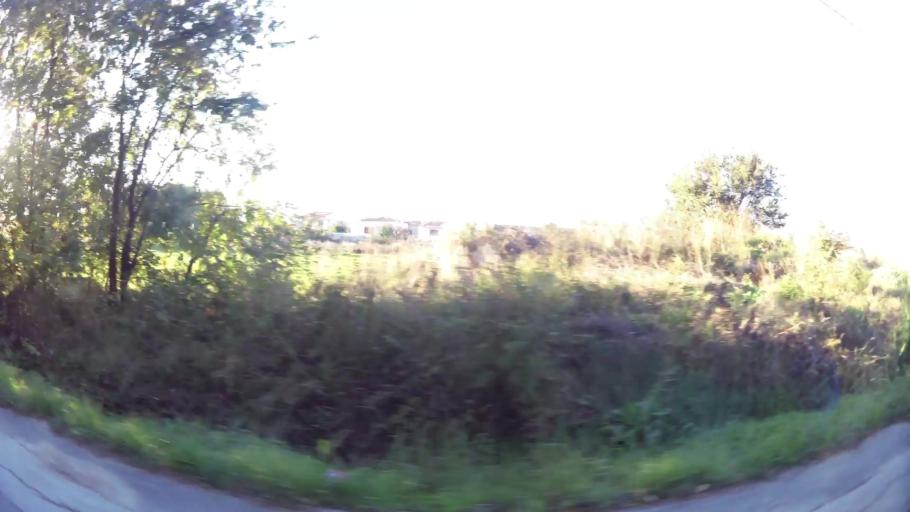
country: GR
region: Attica
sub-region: Nomarchia Anatolikis Attikis
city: Anoixi
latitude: 38.1347
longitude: 23.8557
